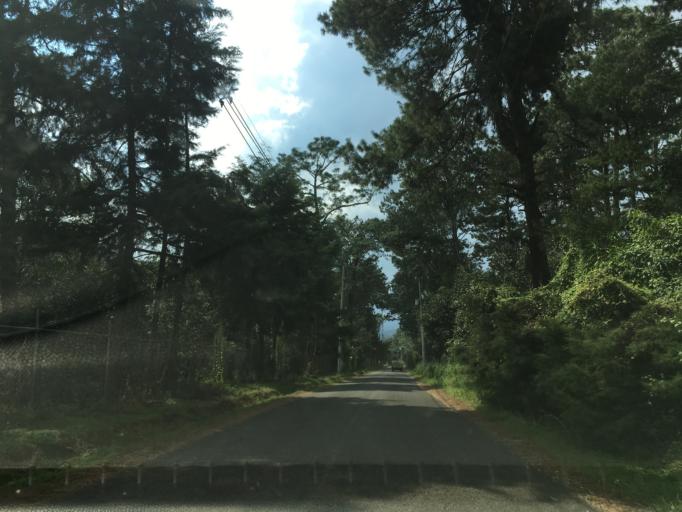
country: MX
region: Michoacan
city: Tingambato
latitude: 19.4618
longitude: -101.8621
